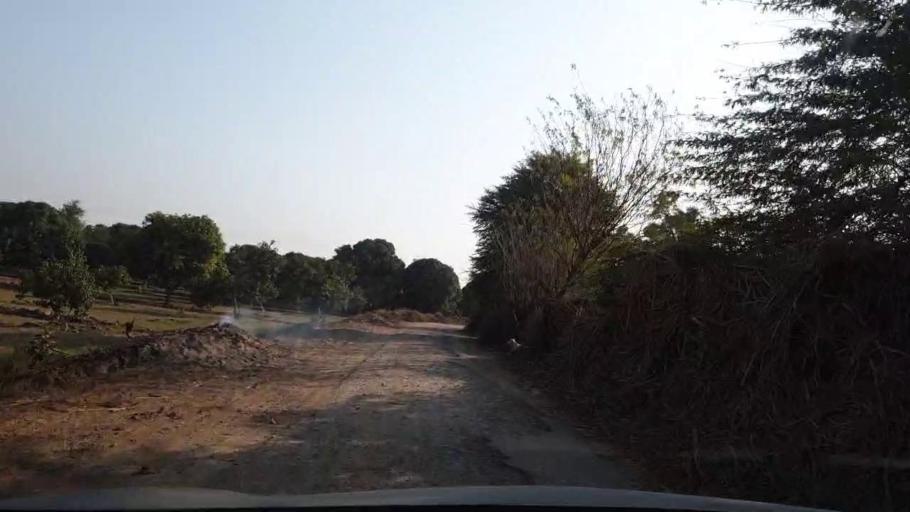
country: PK
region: Sindh
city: Tando Allahyar
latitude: 25.5673
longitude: 68.7643
